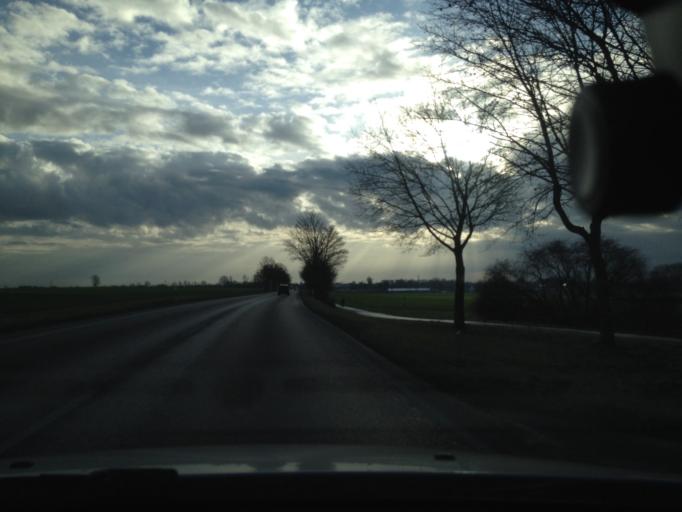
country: DE
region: Bavaria
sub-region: Swabia
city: Grossaitingen
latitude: 48.2173
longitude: 10.7764
